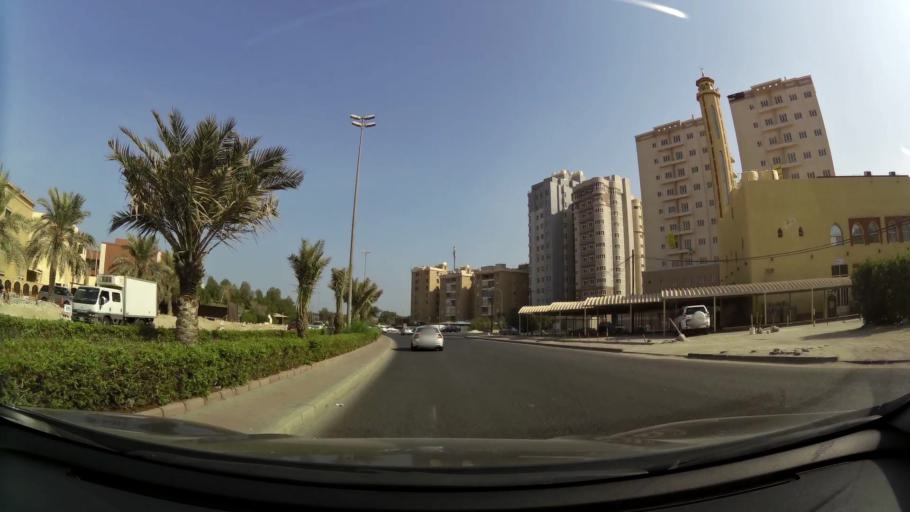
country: KW
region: Al Ahmadi
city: Al Fintas
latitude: 29.1590
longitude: 48.1193
